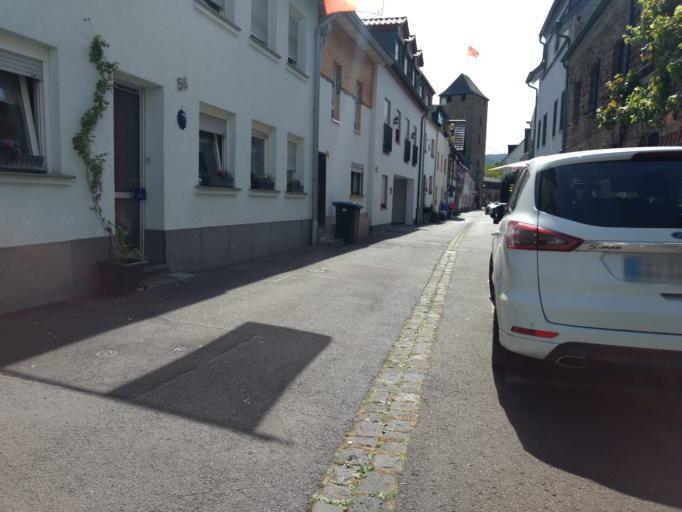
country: DE
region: Rheinland-Pfalz
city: Bad Neuenahr-Ahrweiler
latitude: 50.5414
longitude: 7.0982
